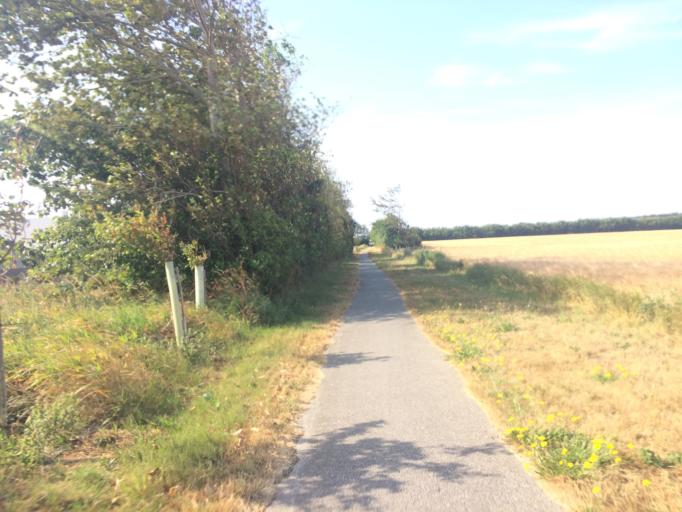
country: DK
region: Central Jutland
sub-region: Holstebro Kommune
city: Vinderup
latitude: 56.6291
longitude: 8.7839
